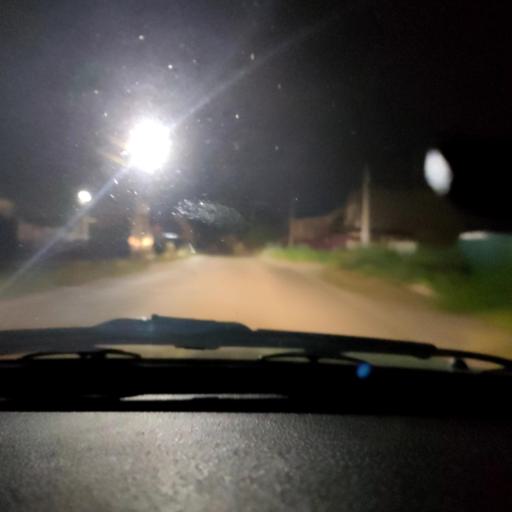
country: RU
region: Voronezj
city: Novaya Usman'
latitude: 51.6382
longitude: 39.4211
